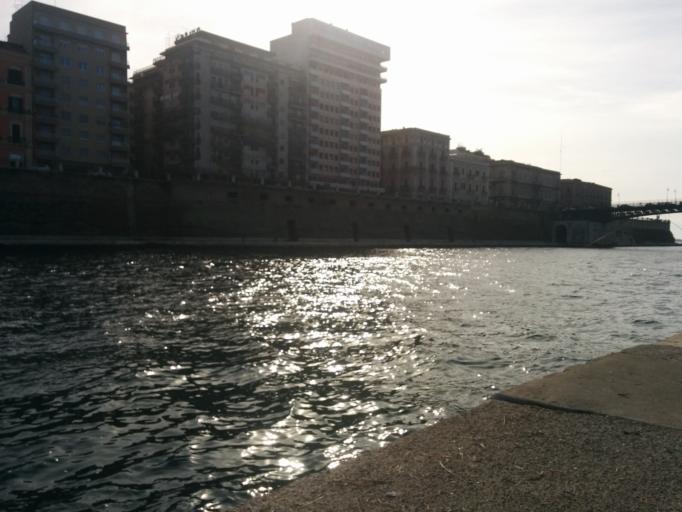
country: IT
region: Apulia
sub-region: Provincia di Taranto
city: Paolo VI
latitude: 40.4752
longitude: 17.2353
